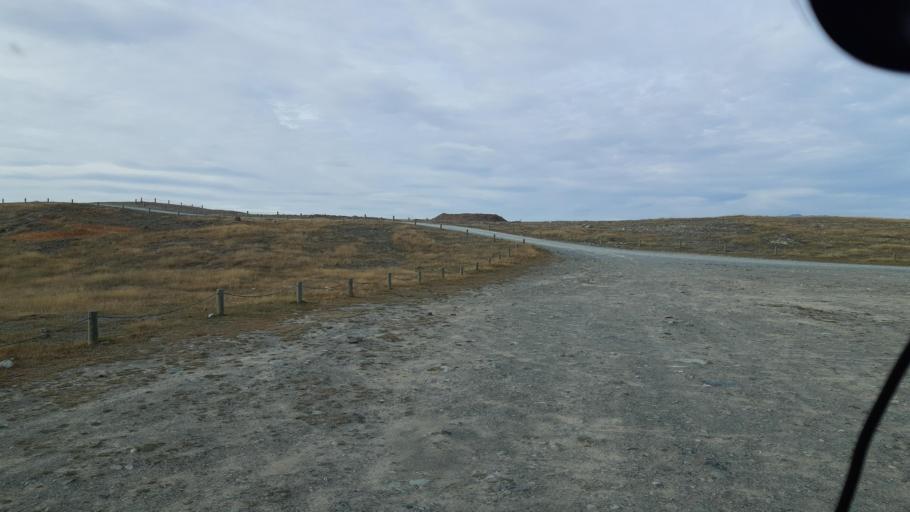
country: NZ
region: Canterbury
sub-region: Timaru District
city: Pleasant Point
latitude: -44.1825
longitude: 170.1523
